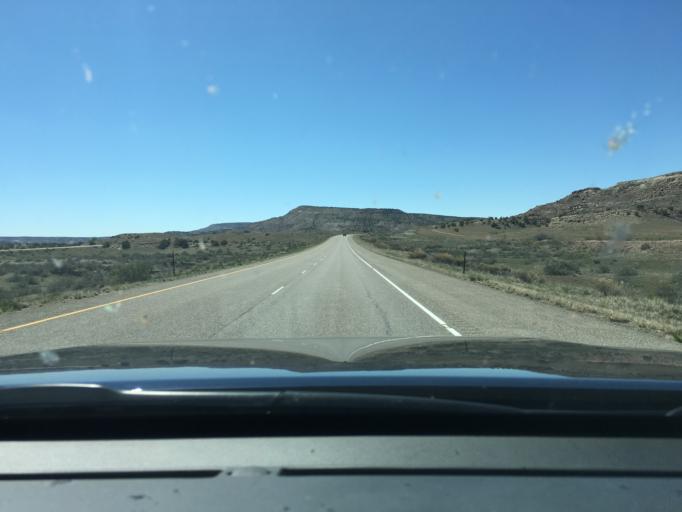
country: US
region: Colorado
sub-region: Mesa County
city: Loma
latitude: 39.1964
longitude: -108.9997
